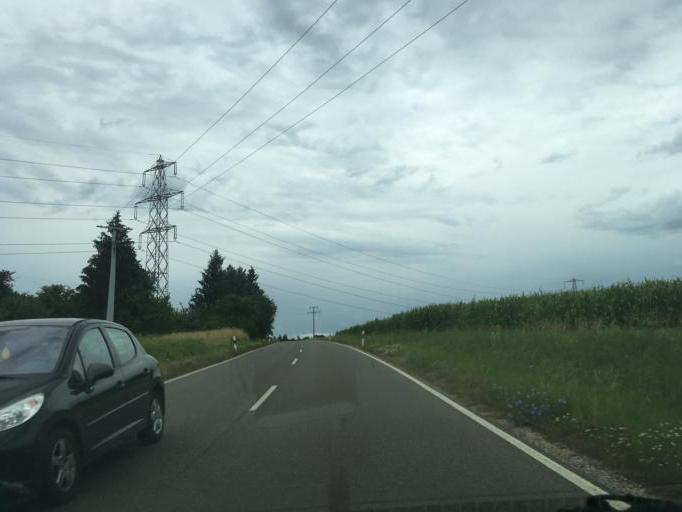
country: DE
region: Baden-Wuerttemberg
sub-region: Tuebingen Region
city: Pliezhausen
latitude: 48.5346
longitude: 9.2175
